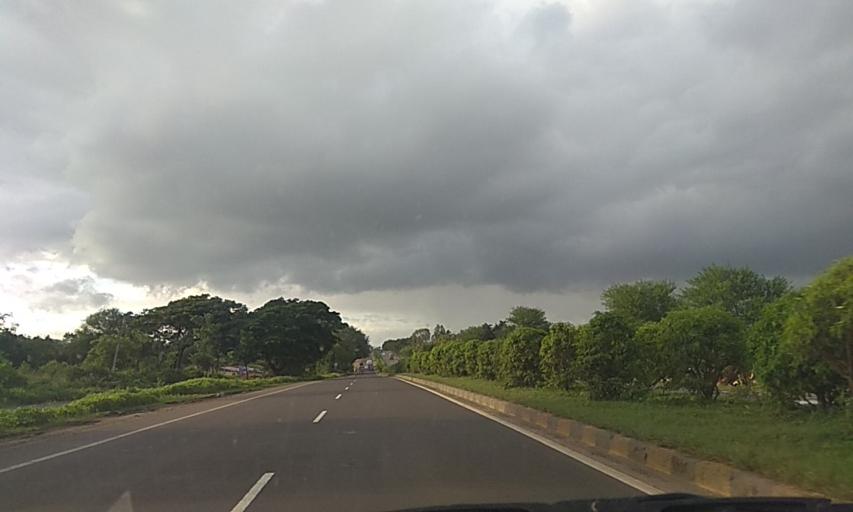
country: IN
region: Maharashtra
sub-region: Satara Division
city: Rahimatpur
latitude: 17.4846
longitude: 74.0848
